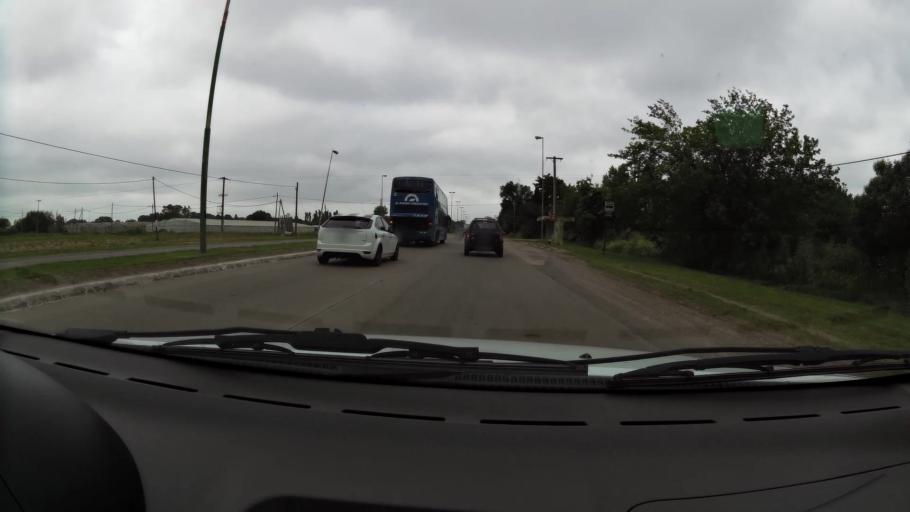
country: AR
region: Buenos Aires
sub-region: Partido de La Plata
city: La Plata
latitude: -35.0184
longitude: -58.0734
